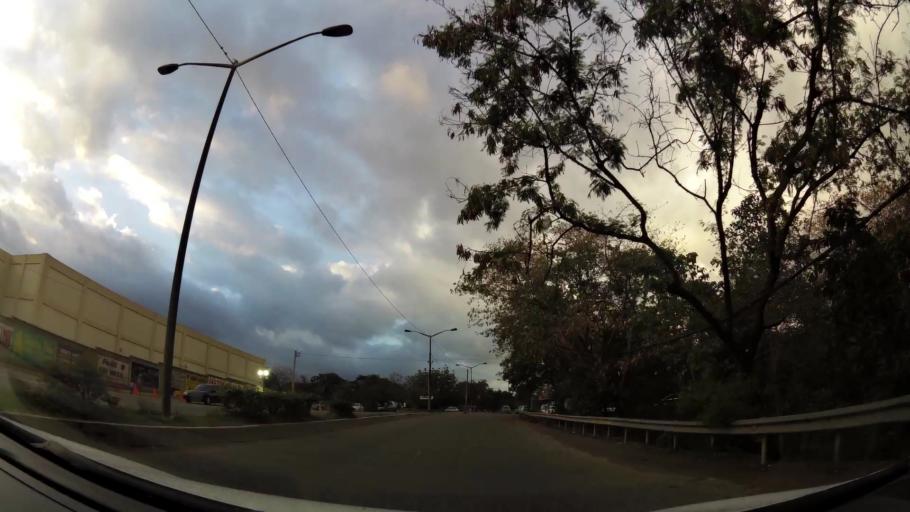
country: DO
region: Santo Domingo
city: Santo Domingo Oeste
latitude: 18.5012
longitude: -69.9991
